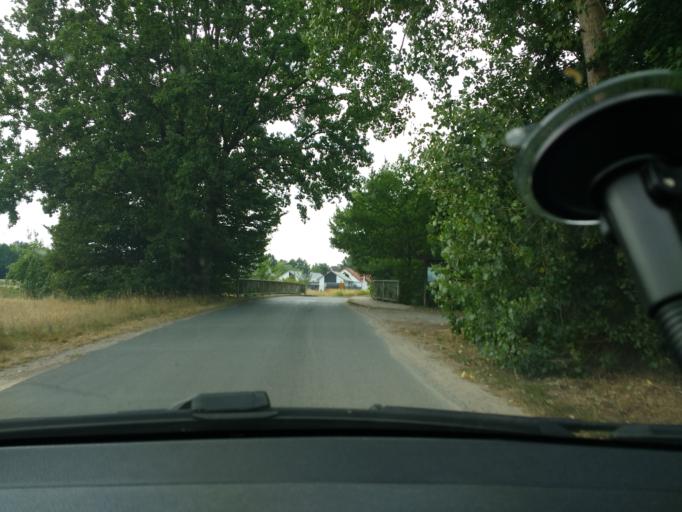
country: DE
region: Lower Saxony
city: Wagenhoff
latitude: 52.5156
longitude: 10.5489
